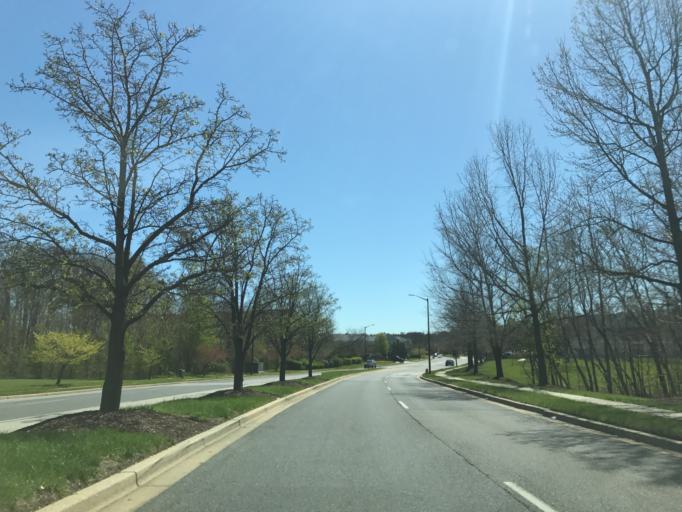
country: US
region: Maryland
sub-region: Anne Arundel County
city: Odenton
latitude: 39.1001
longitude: -76.7185
